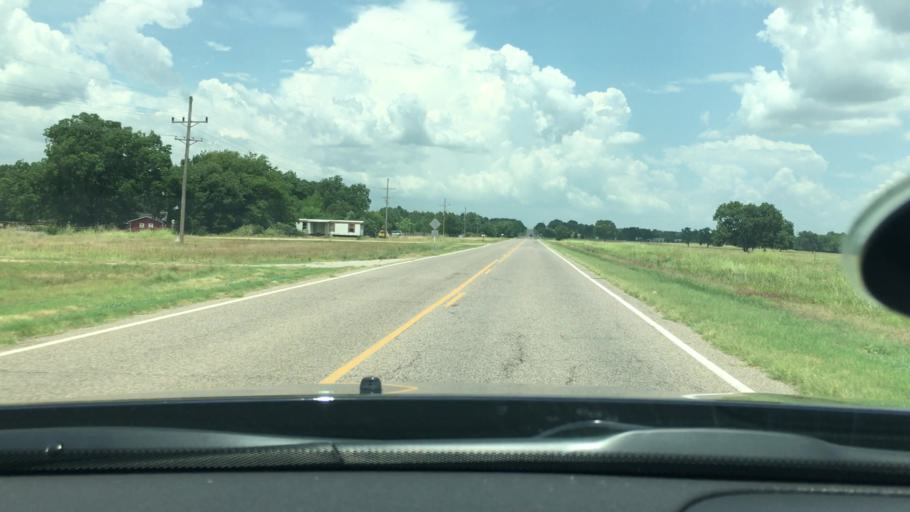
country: US
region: Oklahoma
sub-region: Marshall County
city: Oakland
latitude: 33.9899
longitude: -96.8825
